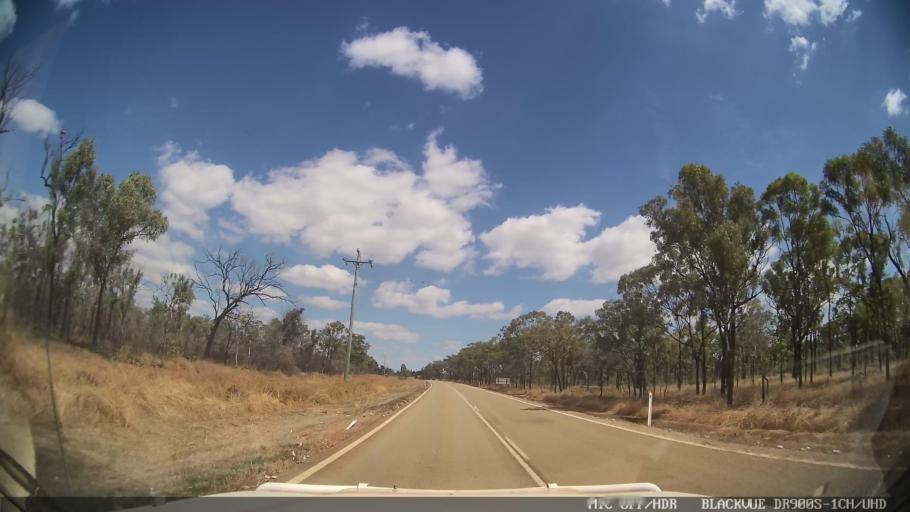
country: AU
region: Queensland
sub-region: Tablelands
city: Ravenshoe
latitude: -18.1351
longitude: 144.8135
